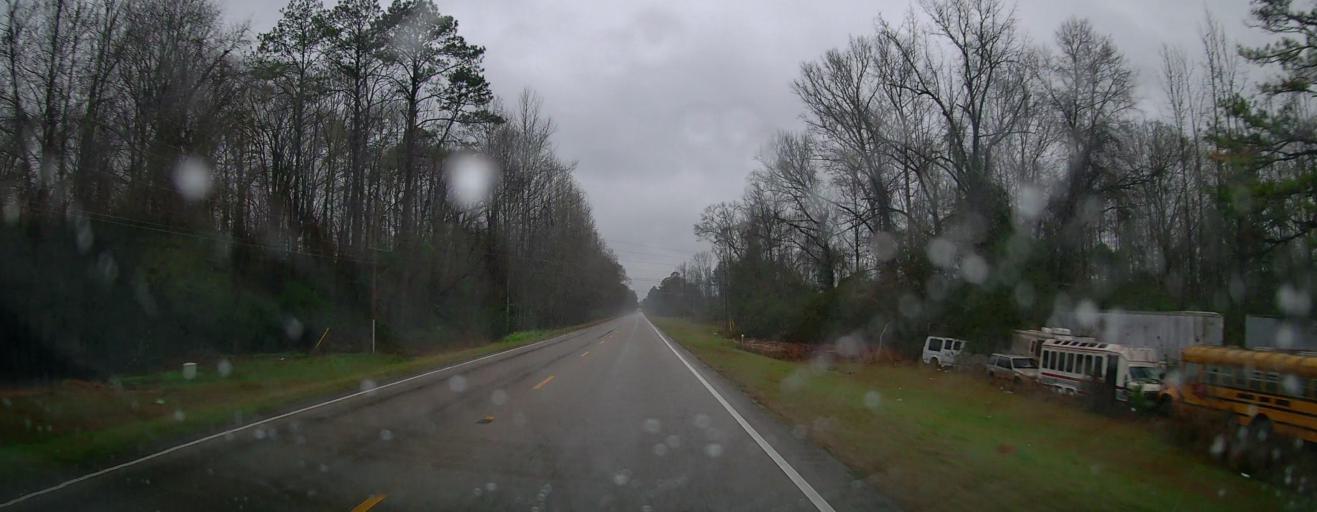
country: US
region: Alabama
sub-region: Autauga County
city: Prattville
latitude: 32.4812
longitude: -86.5316
